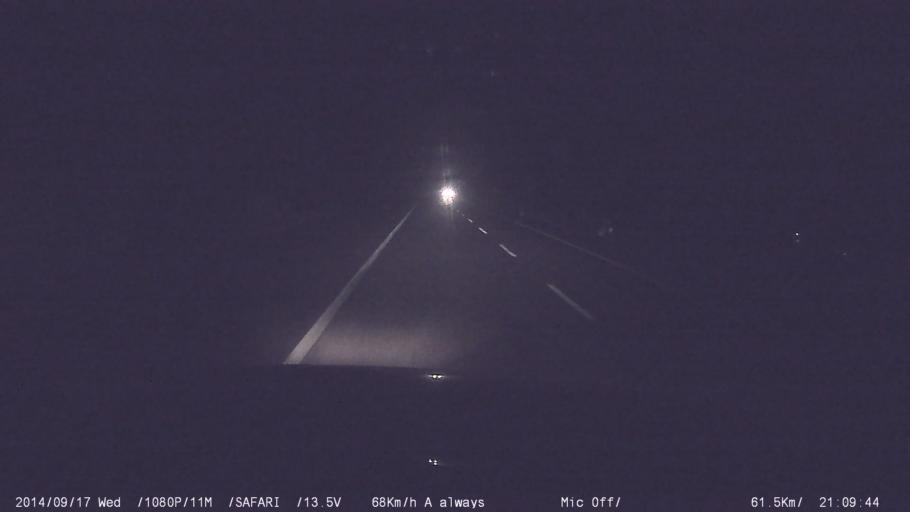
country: IN
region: Kerala
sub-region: Kottayam
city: Changanacheri
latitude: 9.4625
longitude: 76.5343
